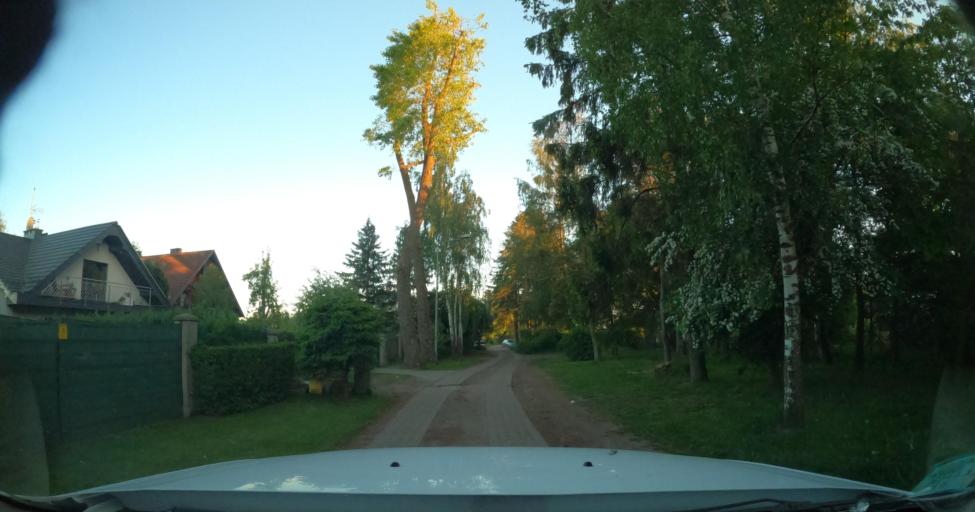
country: PL
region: Pomeranian Voivodeship
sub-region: Slupsk
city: Slupsk
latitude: 54.4719
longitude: 16.9988
